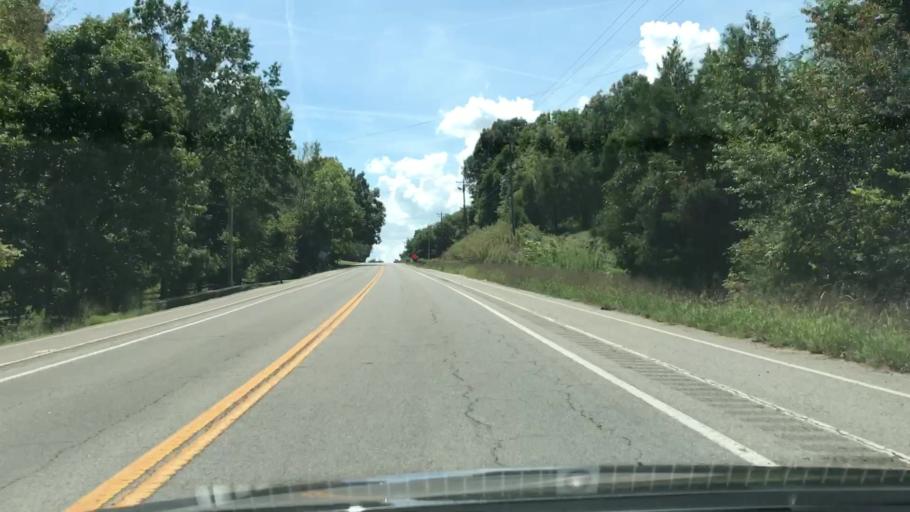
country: US
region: Tennessee
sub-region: Sumner County
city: White House
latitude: 36.4869
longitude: -86.6453
